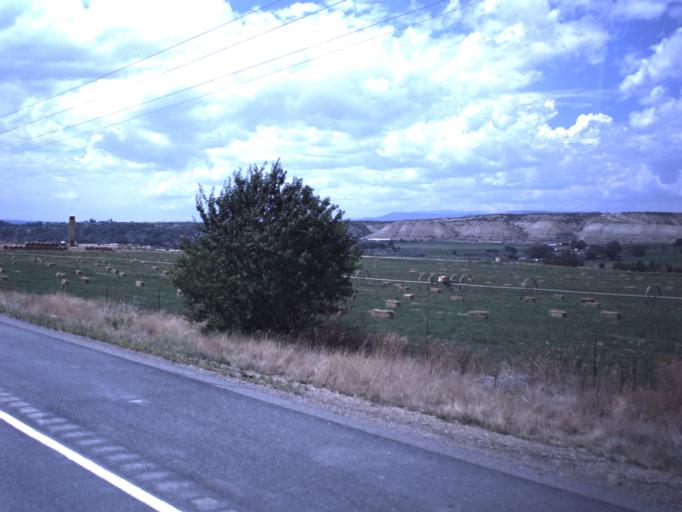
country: US
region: Utah
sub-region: Duchesne County
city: Duchesne
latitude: 40.1706
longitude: -110.3462
